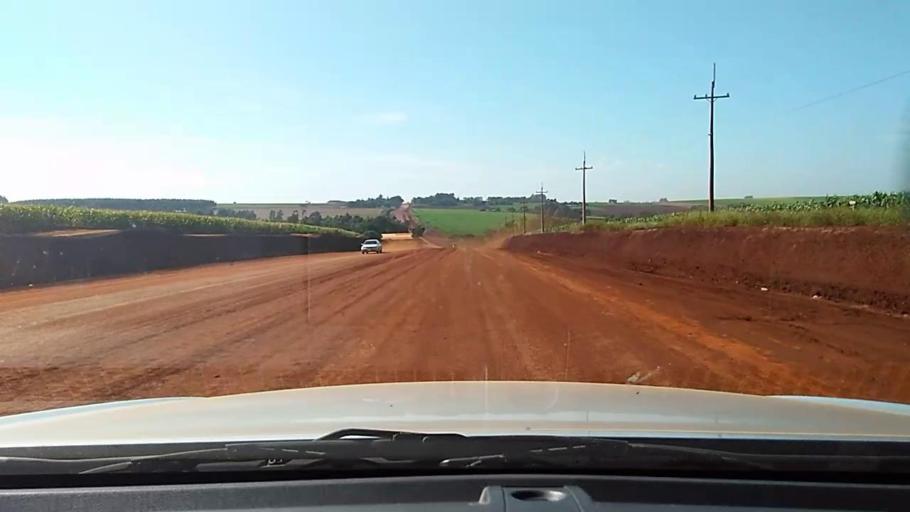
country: PY
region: Alto Parana
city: Naranjal
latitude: -25.9221
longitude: -55.4113
